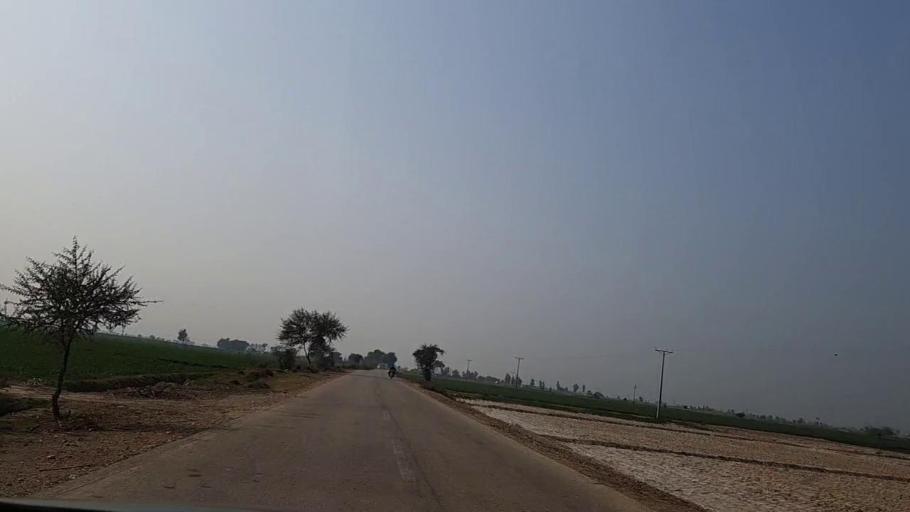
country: PK
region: Sindh
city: Sakrand
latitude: 26.1369
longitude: 68.1787
